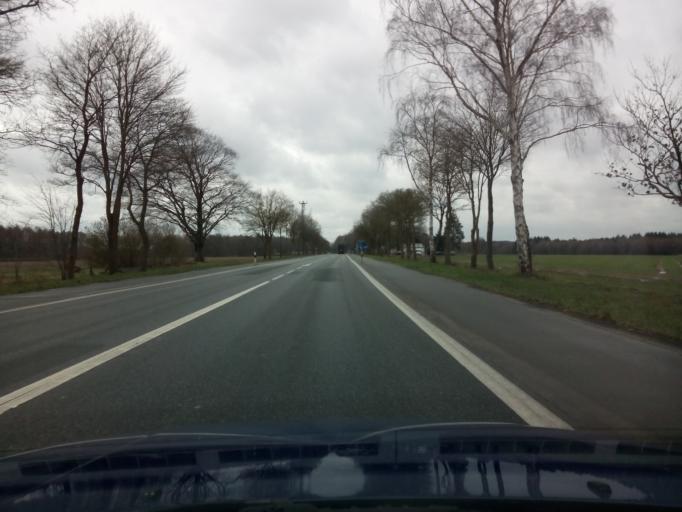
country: DE
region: Lower Saxony
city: Wildeshausen
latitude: 52.9190
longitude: 8.4585
